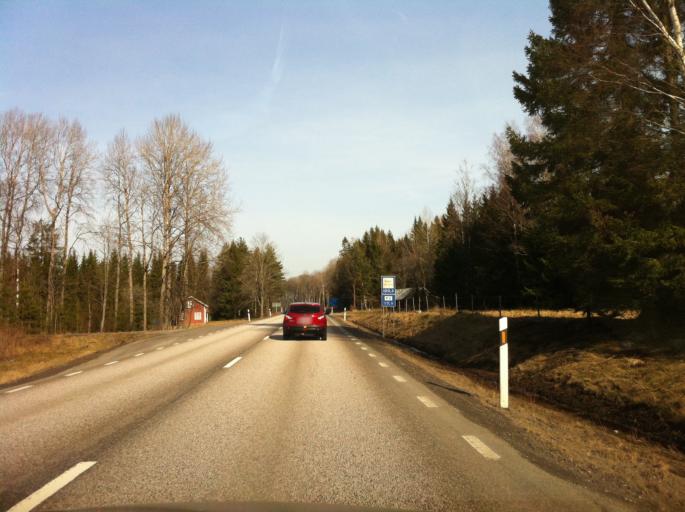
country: SE
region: Joenkoeping
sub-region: Mullsjo Kommun
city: Mullsjoe
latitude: 58.0280
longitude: 13.8340
